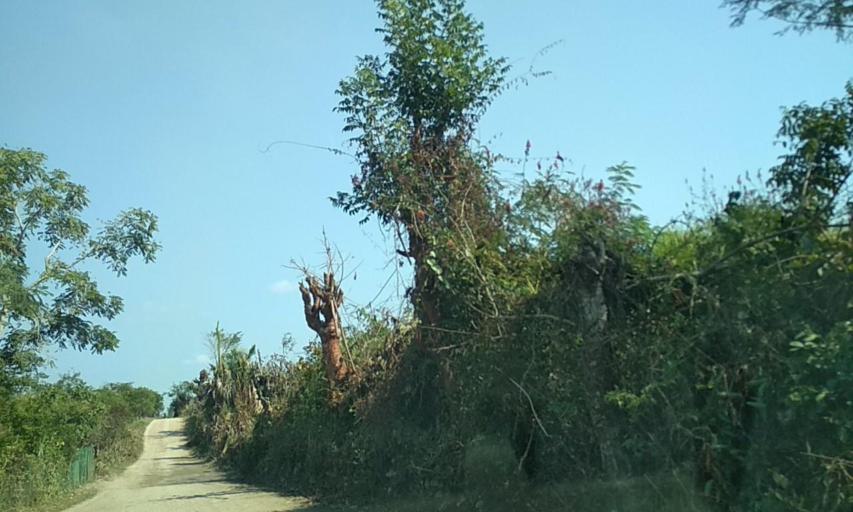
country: MX
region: Veracruz
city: Gutierrez Zamora
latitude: 20.3770
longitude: -97.1477
